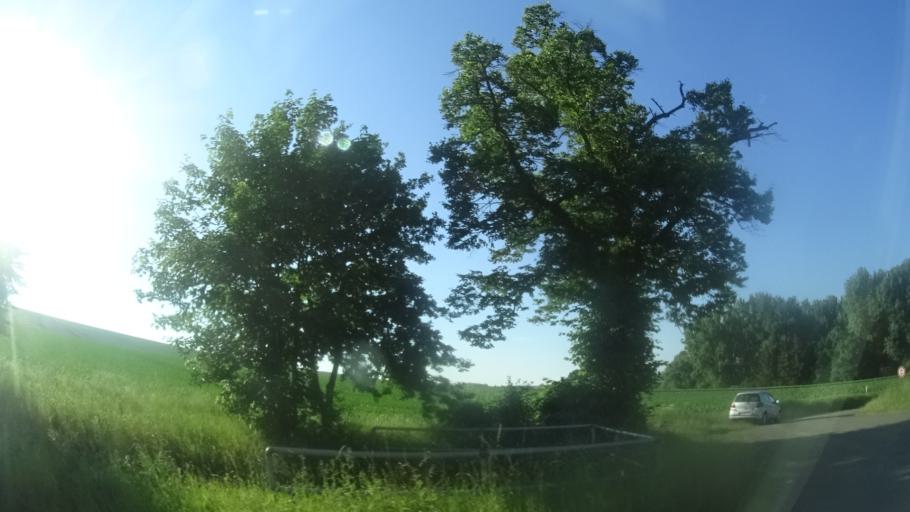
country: DE
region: Lower Saxony
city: Baddeckenstedt
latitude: 52.0858
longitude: 10.2049
